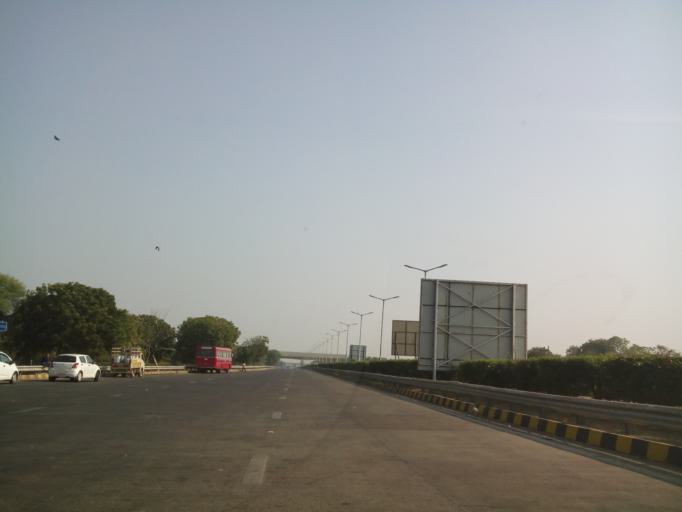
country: IN
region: Gujarat
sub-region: Ahmadabad
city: Ahmedabad
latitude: 22.9754
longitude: 72.6511
